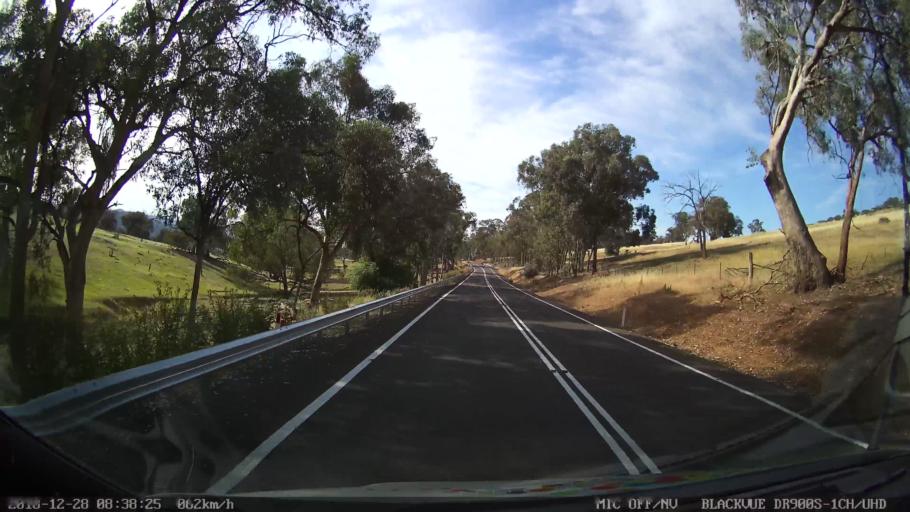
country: AU
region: New South Wales
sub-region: Blayney
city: Blayney
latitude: -34.0034
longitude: 149.3151
